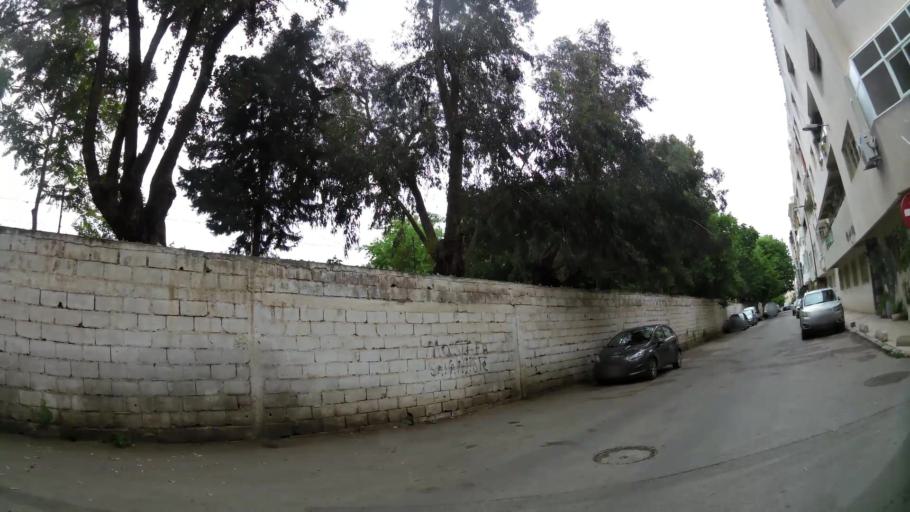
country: MA
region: Fes-Boulemane
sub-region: Fes
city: Fes
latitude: 34.0273
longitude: -4.9973
